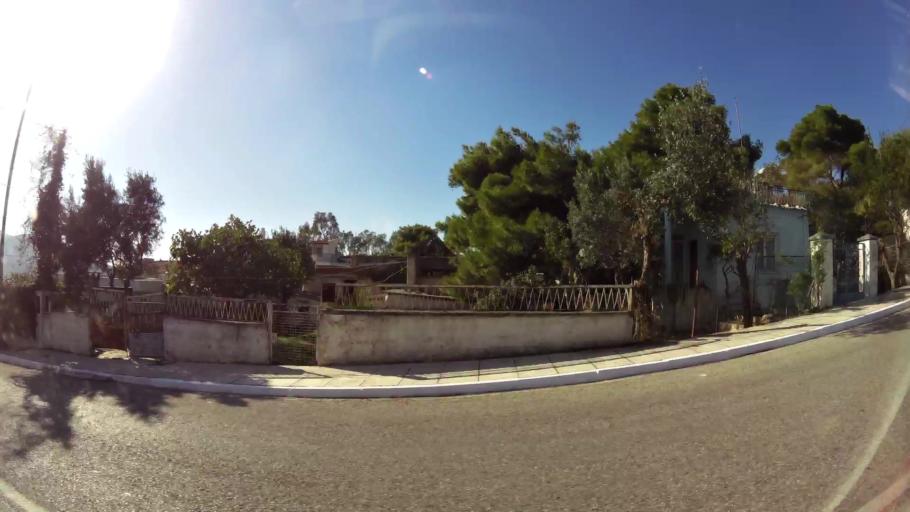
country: GR
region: Attica
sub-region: Nomarchia Anatolikis Attikis
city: Anthousa
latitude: 38.0286
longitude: 23.8739
